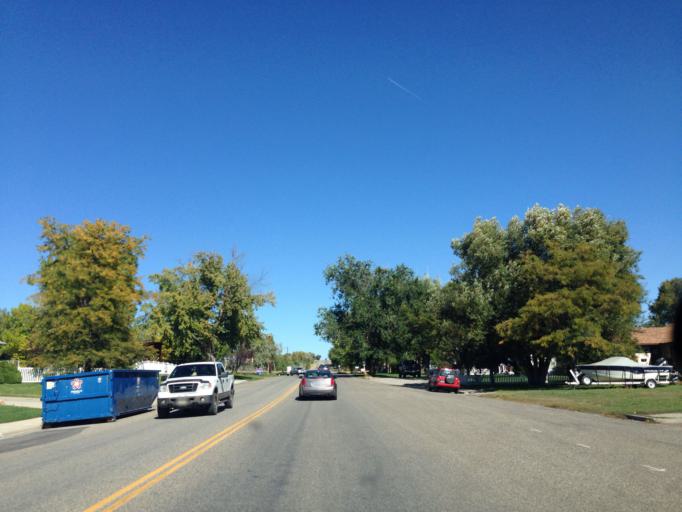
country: US
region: Montana
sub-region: Yellowstone County
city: Laurel
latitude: 45.6813
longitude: -108.7716
